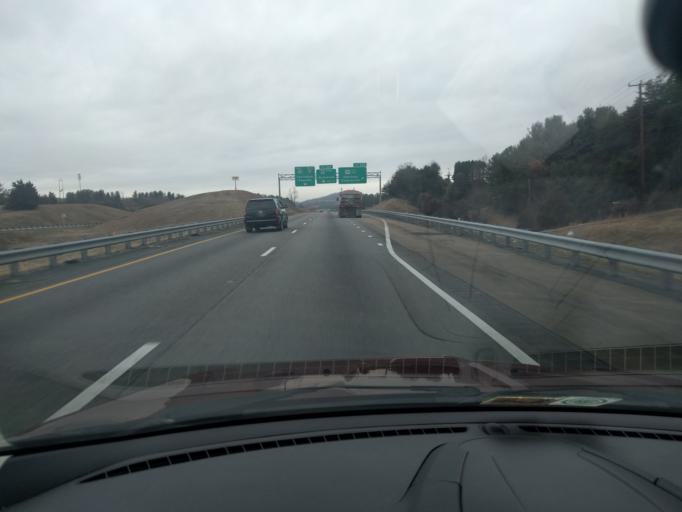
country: US
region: Virginia
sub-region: City of Staunton
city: Staunton
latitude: 38.1319
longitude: -79.0317
